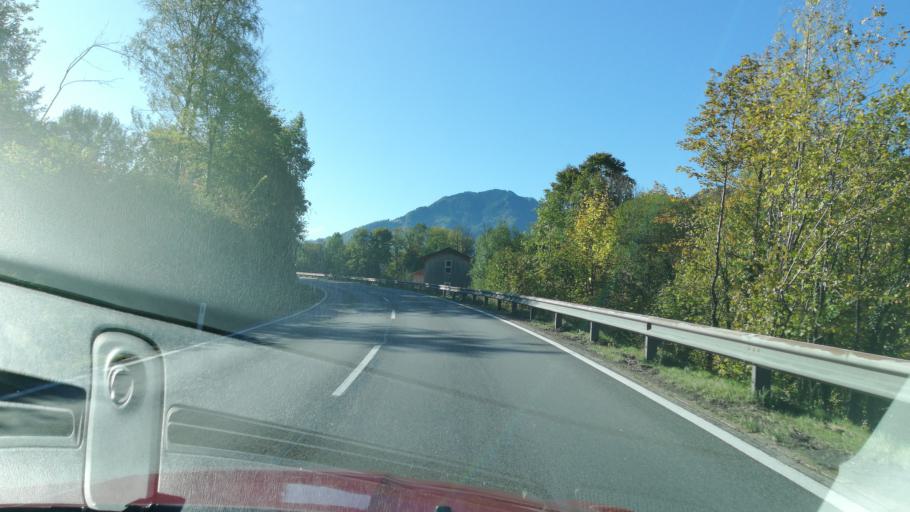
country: AT
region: Upper Austria
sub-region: Politischer Bezirk Steyr-Land
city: Weyer
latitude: 47.8314
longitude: 14.6442
